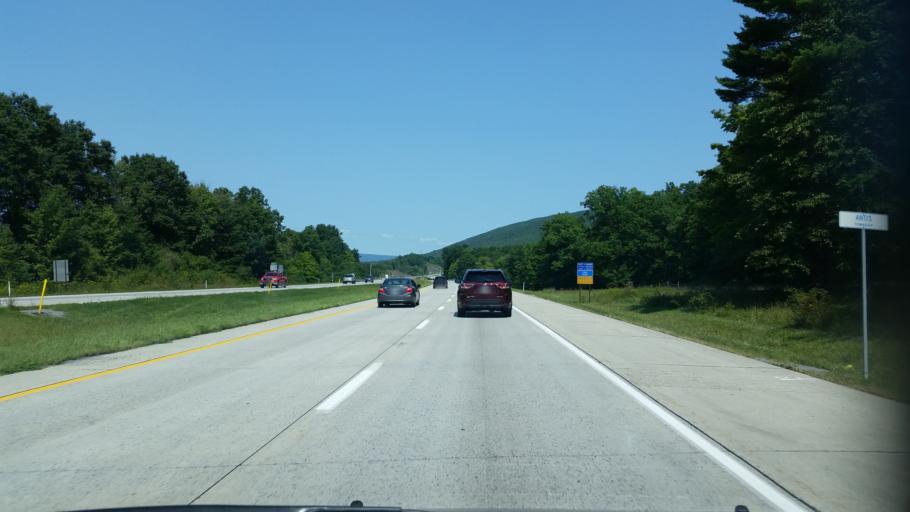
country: US
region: Pennsylvania
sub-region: Blair County
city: Greenwood
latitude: 40.5535
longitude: -78.3331
